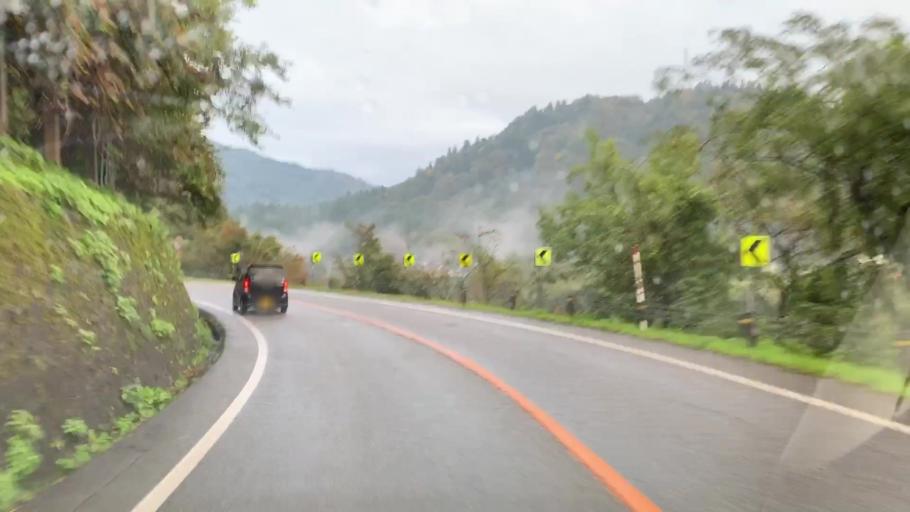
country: JP
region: Toyama
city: Kamiichi
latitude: 36.5732
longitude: 137.3588
